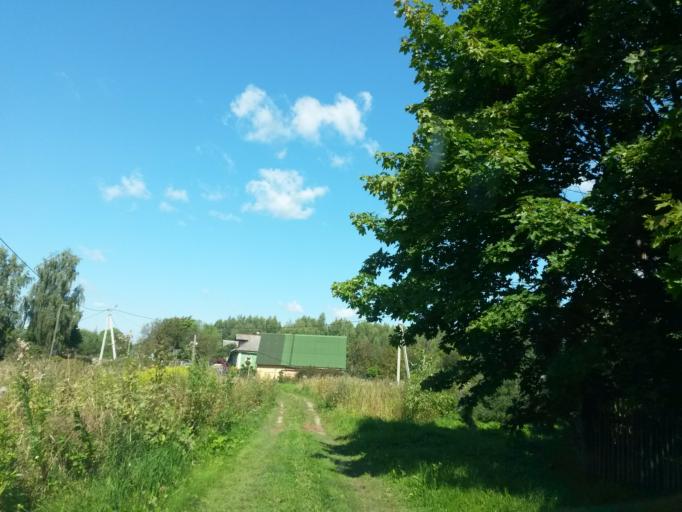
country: RU
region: Jaroslavl
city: Burmakino
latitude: 57.3858
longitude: 40.2137
